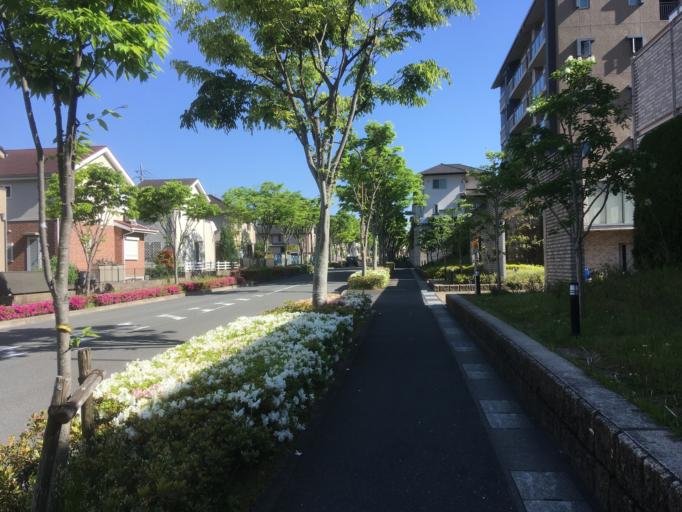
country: JP
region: Nara
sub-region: Ikoma-shi
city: Ikoma
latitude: 34.7199
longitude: 135.7161
